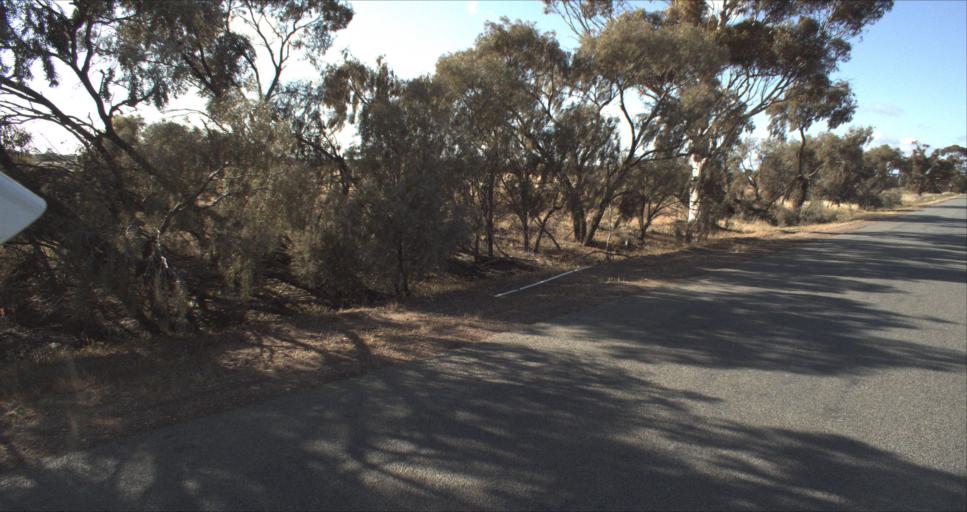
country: AU
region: New South Wales
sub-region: Leeton
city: Leeton
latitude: -34.5169
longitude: 146.3913
